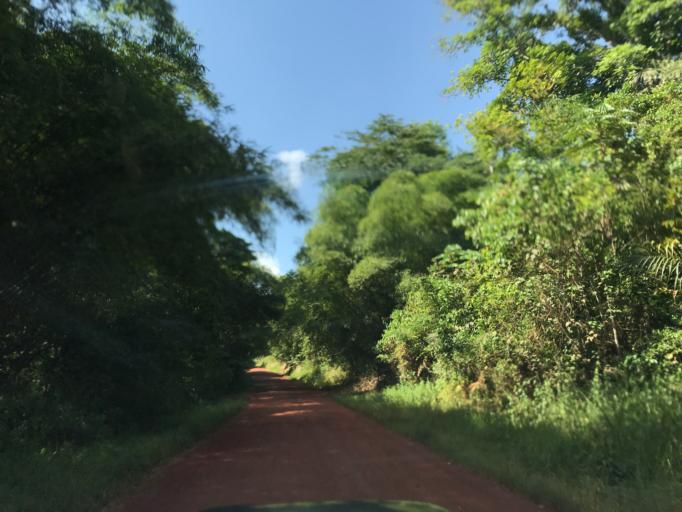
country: CD
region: Eastern Province
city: Kisangani
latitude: 1.2553
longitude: 25.2776
